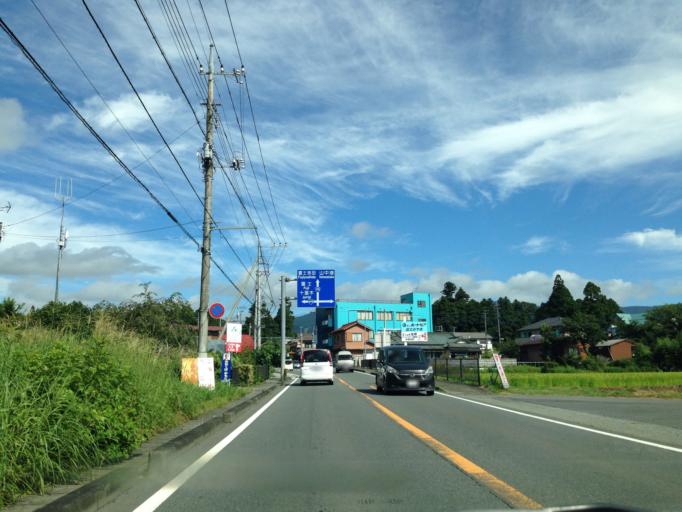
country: JP
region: Shizuoka
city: Gotemba
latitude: 35.3225
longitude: 138.9107
